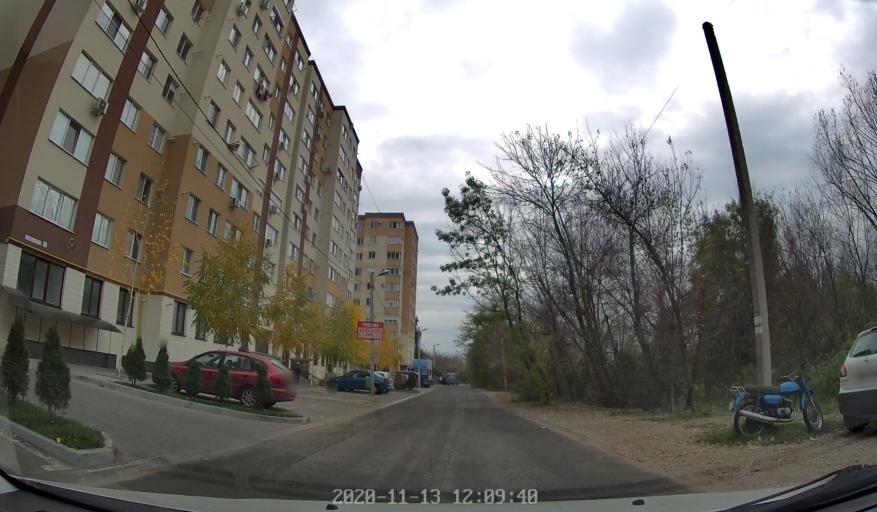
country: MD
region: Chisinau
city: Chisinau
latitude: 46.9580
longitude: 28.8368
